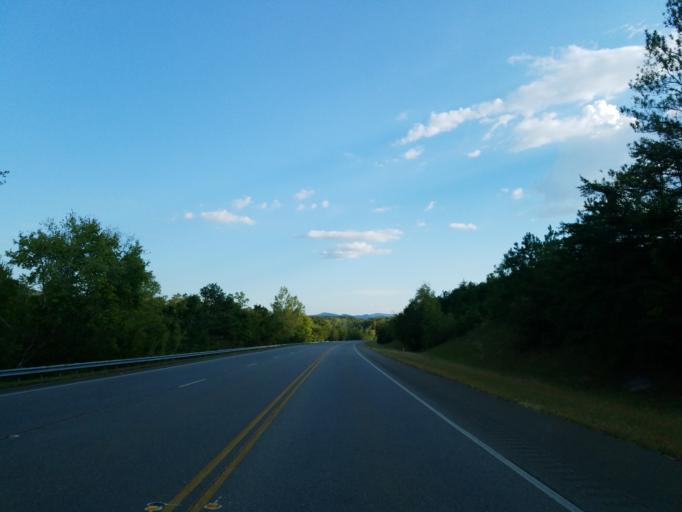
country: US
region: Georgia
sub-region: Murray County
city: Chatsworth
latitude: 34.6713
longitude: -84.7234
